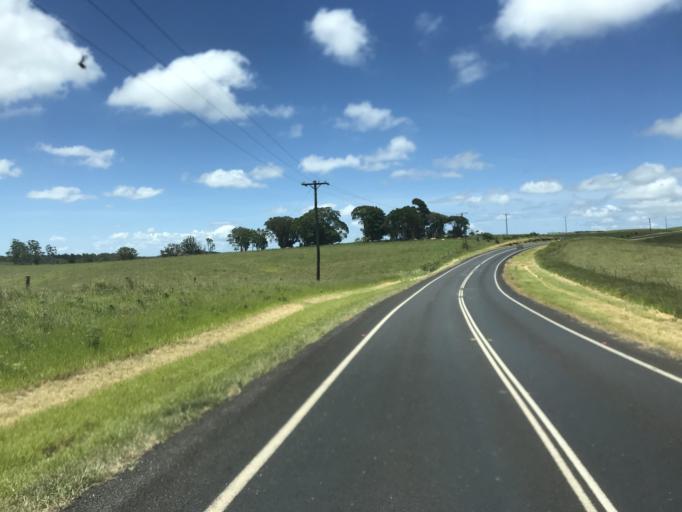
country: AU
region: Queensland
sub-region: Tablelands
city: Ravenshoe
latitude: -17.4926
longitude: 145.4744
